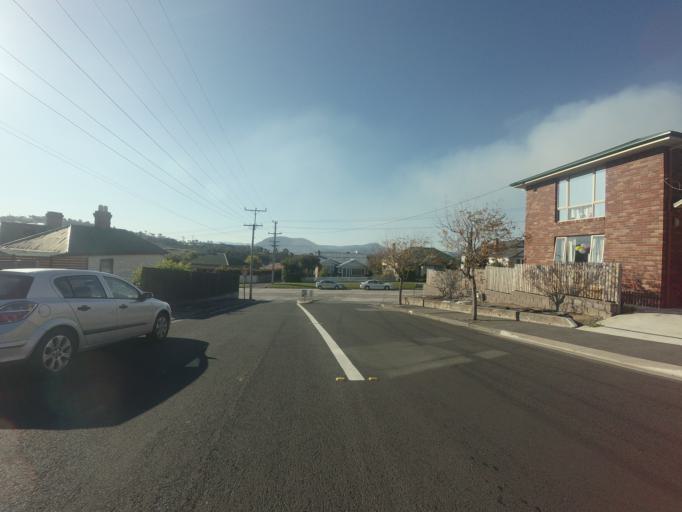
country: AU
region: Tasmania
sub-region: Hobart
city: New Town
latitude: -42.8652
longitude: 147.2941
